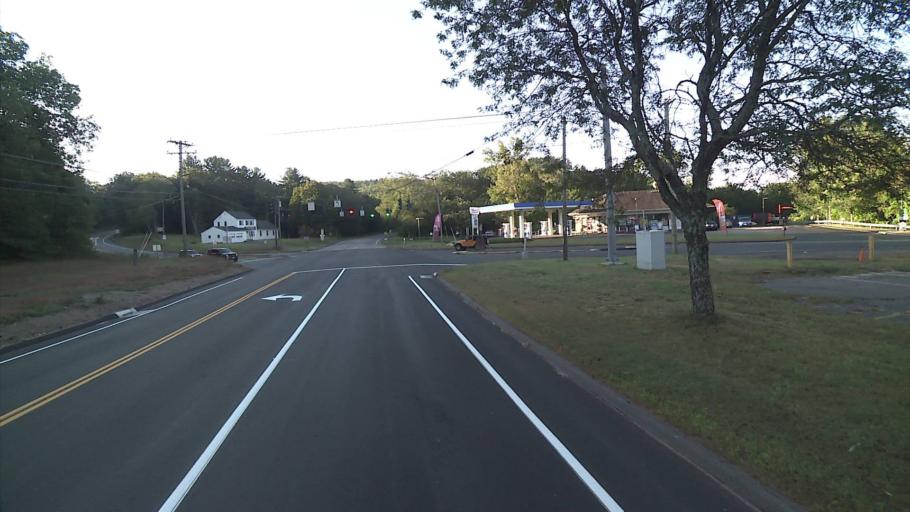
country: US
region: Connecticut
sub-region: Tolland County
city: Storrs
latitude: 41.8356
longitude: -72.3069
